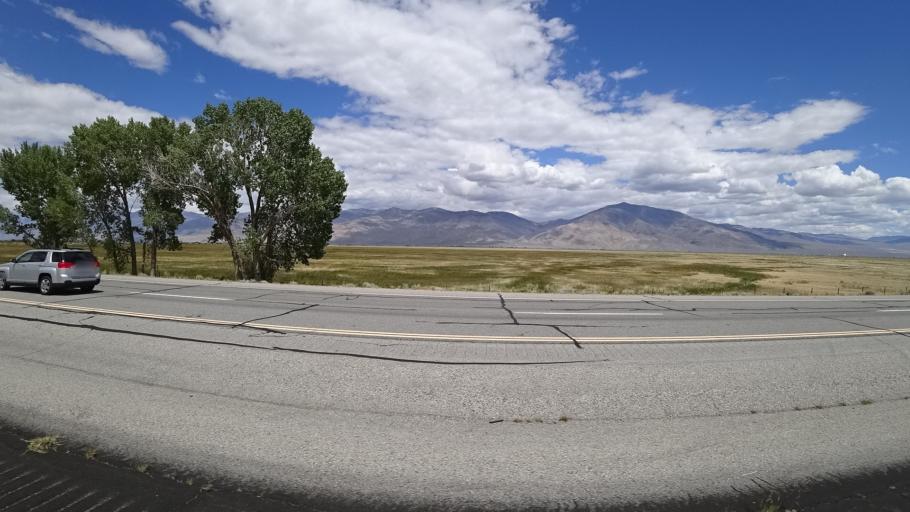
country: US
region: California
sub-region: Inyo County
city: Bishop
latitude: 37.2689
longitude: -118.3665
